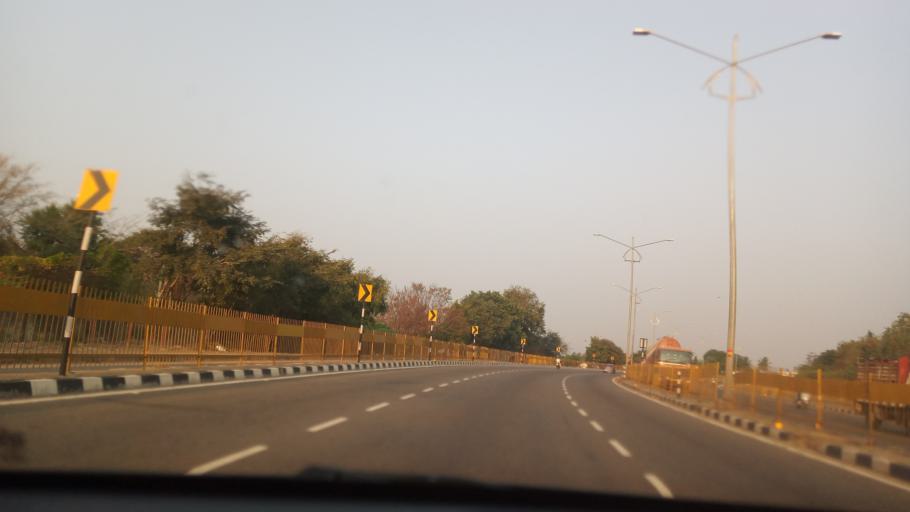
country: IN
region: Tamil Nadu
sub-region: Vellore
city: Vellore
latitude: 12.9224
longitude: 79.0983
